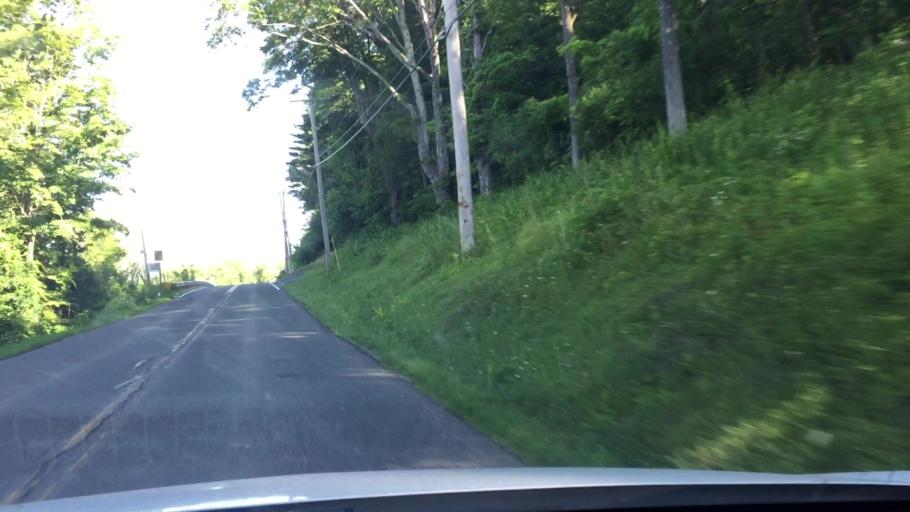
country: US
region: Massachusetts
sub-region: Berkshire County
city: Lee
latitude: 42.2686
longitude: -73.2336
